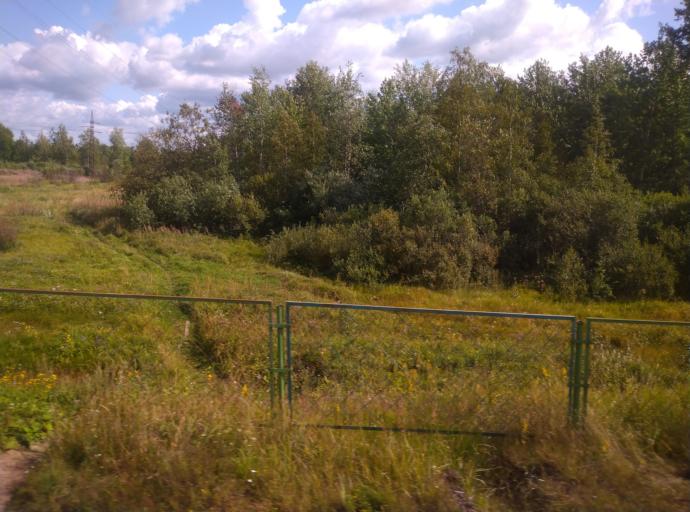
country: RU
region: Leningrad
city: Krasnyy Bor
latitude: 59.6751
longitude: 30.7089
